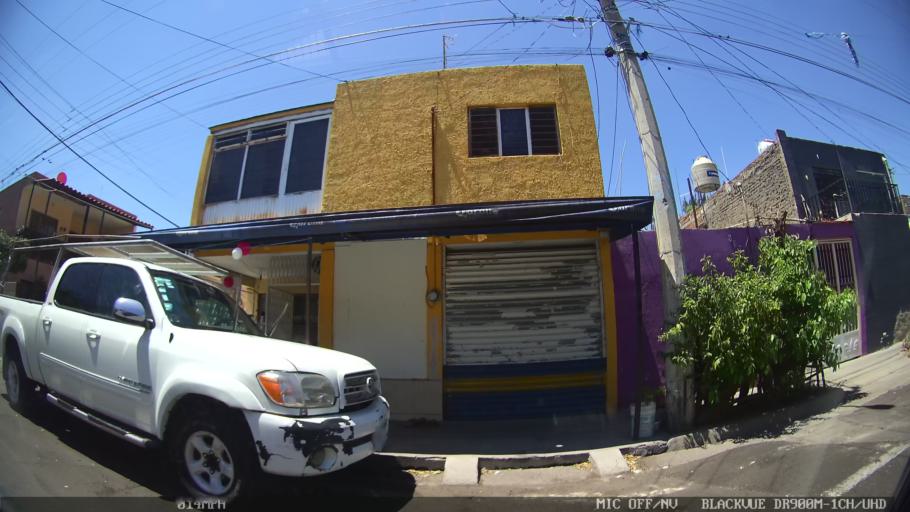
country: MX
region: Jalisco
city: Tlaquepaque
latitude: 20.6829
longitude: -103.2817
